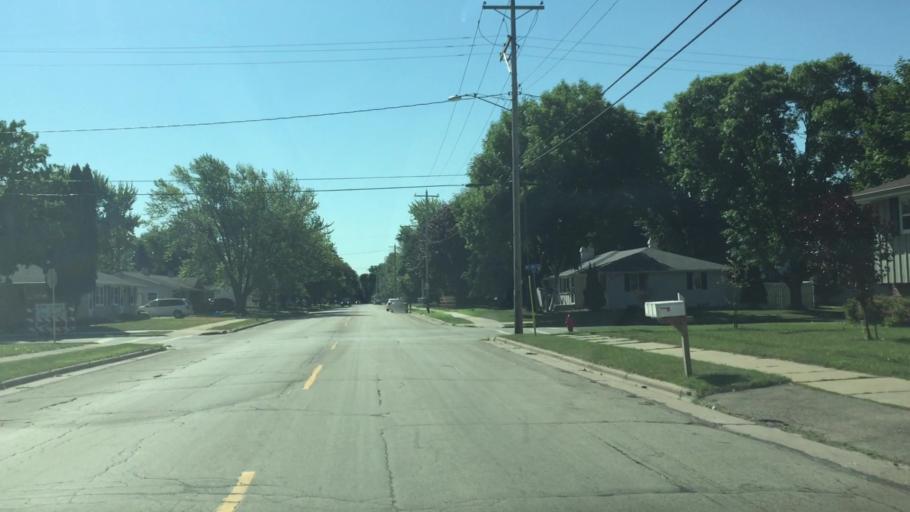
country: US
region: Wisconsin
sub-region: Winnebago County
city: Menasha
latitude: 44.2212
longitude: -88.4246
